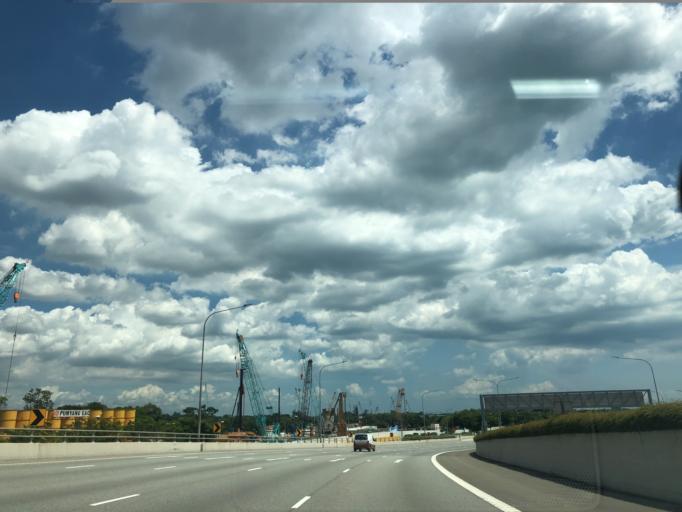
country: SG
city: Singapore
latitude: 1.2741
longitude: 103.8508
